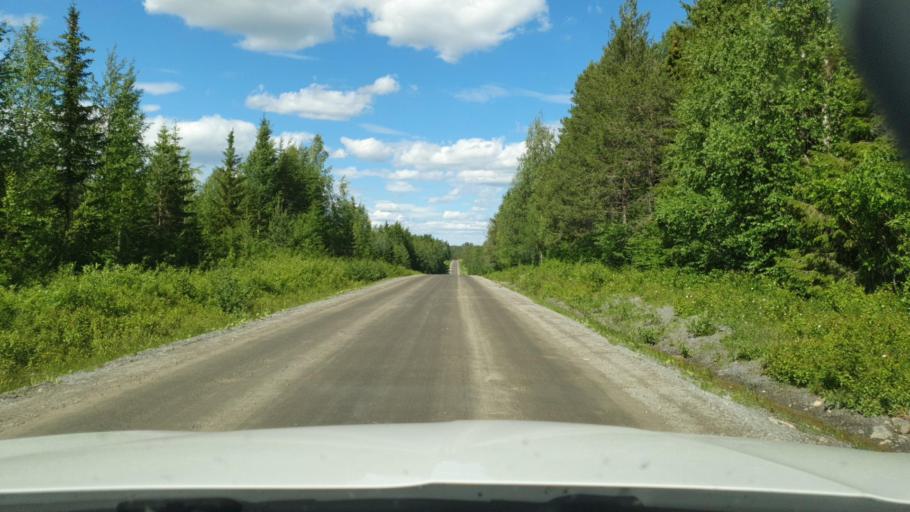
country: SE
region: Vaesterbotten
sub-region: Skelleftea Kommun
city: Forsbacka
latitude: 64.7768
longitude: 20.5159
